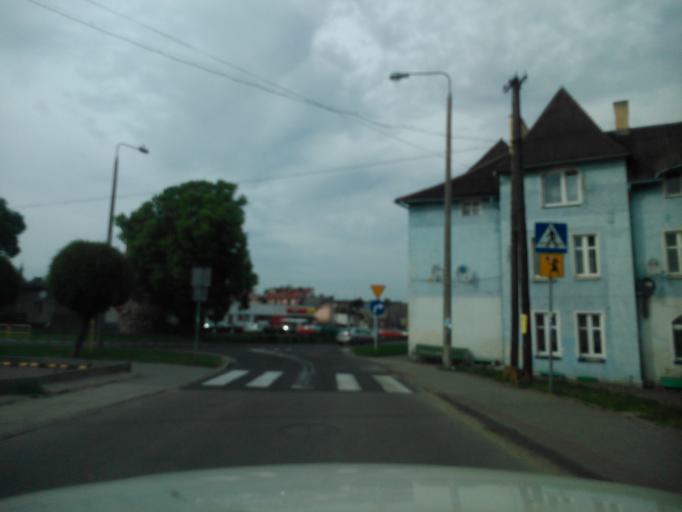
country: PL
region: Kujawsko-Pomorskie
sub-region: Powiat golubsko-dobrzynski
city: Kowalewo Pomorskie
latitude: 53.1523
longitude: 18.8990
